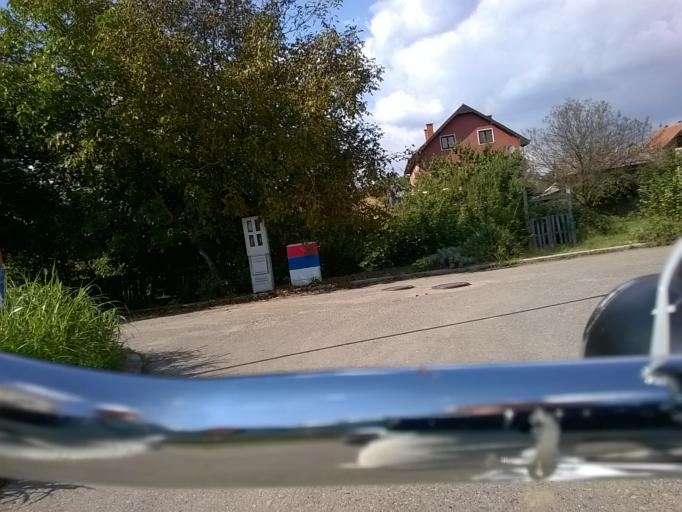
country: RS
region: Autonomna Pokrajina Vojvodina
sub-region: Juznobanatski Okrug
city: Pancevo
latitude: 44.8802
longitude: 20.6385
